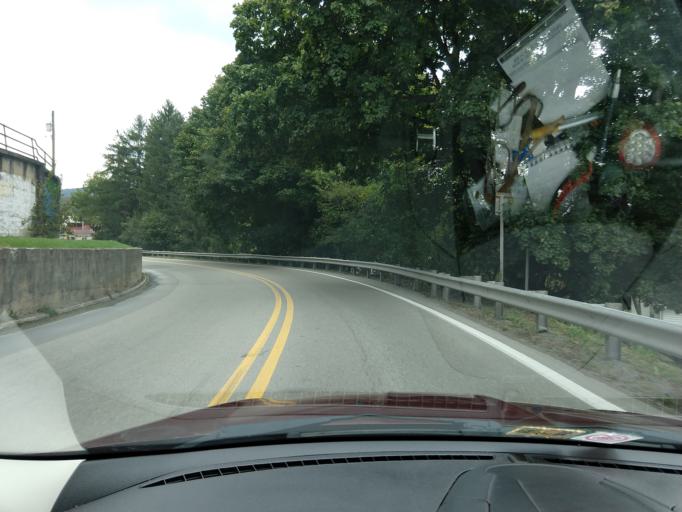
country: US
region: West Virginia
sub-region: Randolph County
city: Elkins
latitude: 38.9276
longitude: -79.8577
